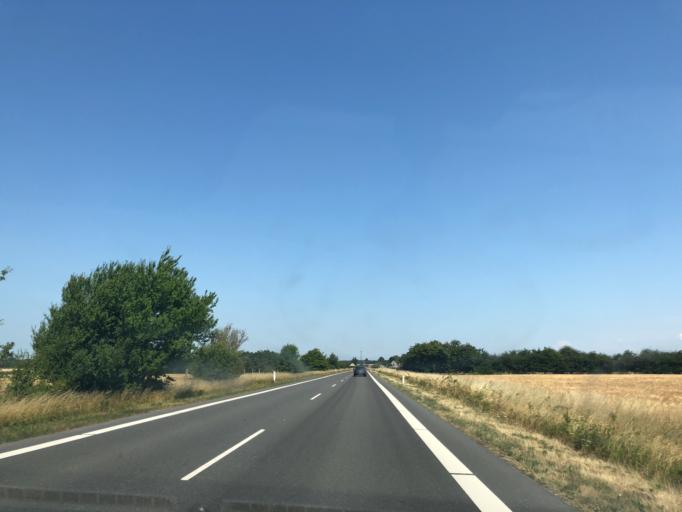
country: DK
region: Zealand
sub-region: Slagelse Kommune
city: Skaelskor
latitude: 55.2320
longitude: 11.3122
